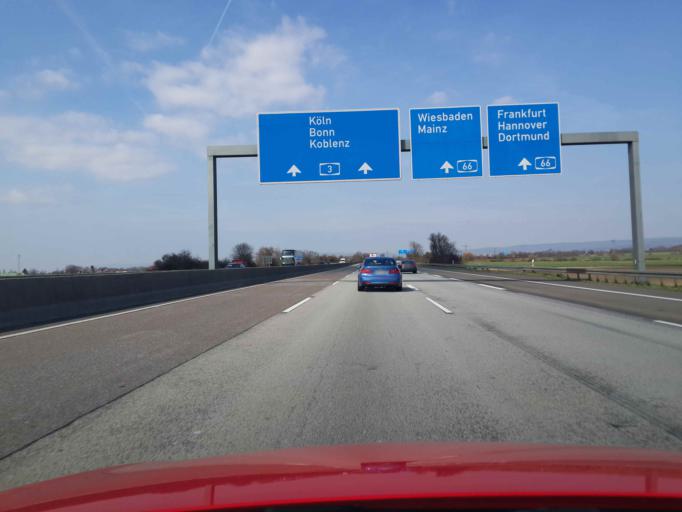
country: DE
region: Hesse
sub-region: Regierungsbezirk Darmstadt
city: Florsheim
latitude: 50.0454
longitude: 8.4038
